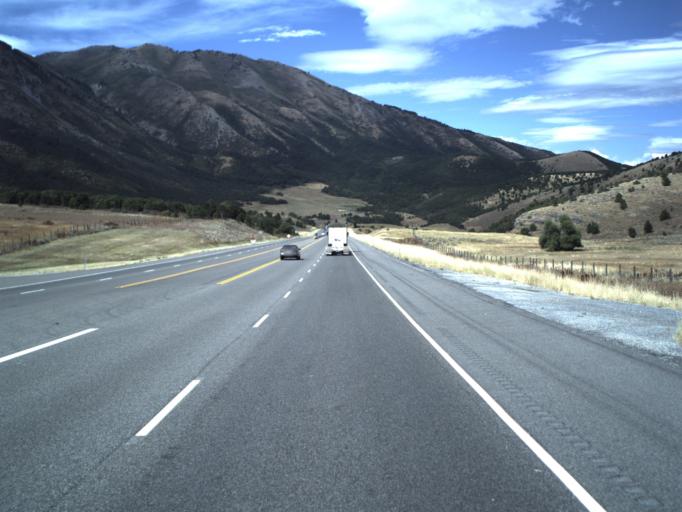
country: US
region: Utah
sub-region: Cache County
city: Wellsville
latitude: 41.5843
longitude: -111.9751
